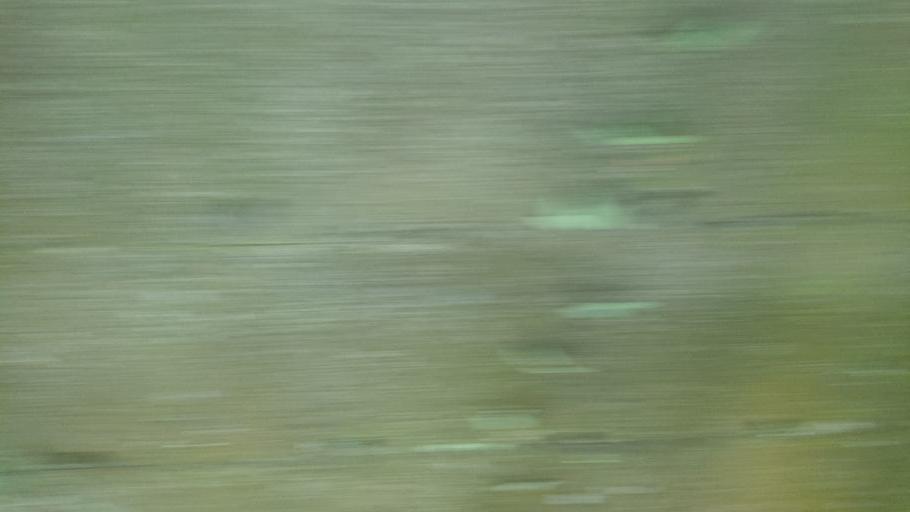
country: TW
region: Taiwan
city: Daxi
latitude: 24.8806
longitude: 121.3807
